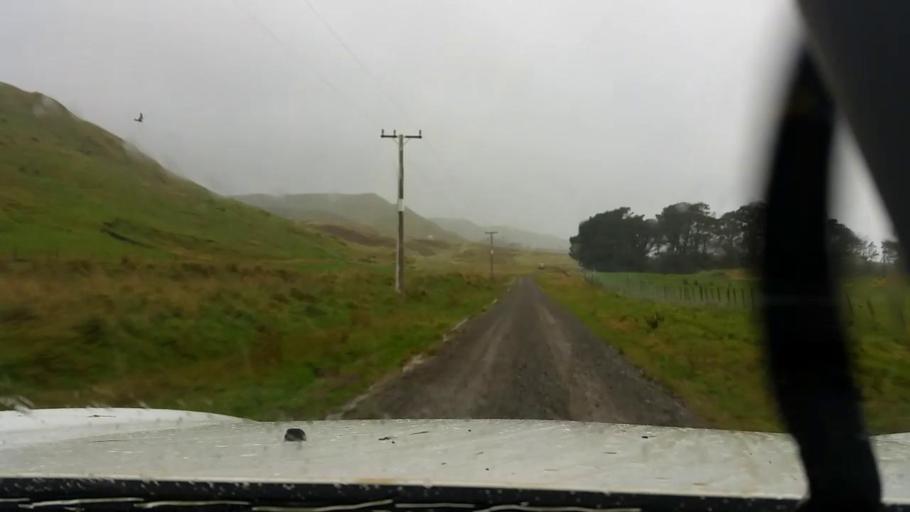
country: NZ
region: Wellington
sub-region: Masterton District
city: Masterton
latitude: -41.2543
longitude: 175.9100
